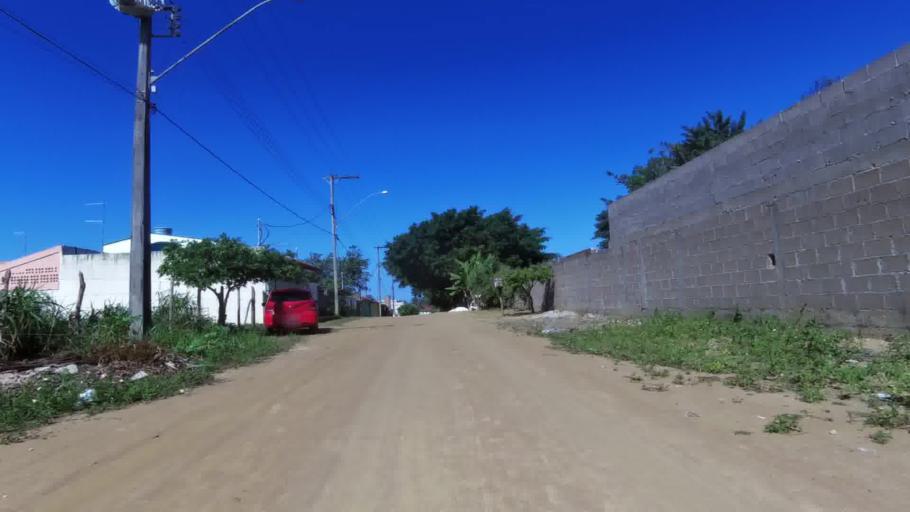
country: BR
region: Espirito Santo
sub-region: Guarapari
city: Guarapari
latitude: -20.7339
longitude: -40.5460
